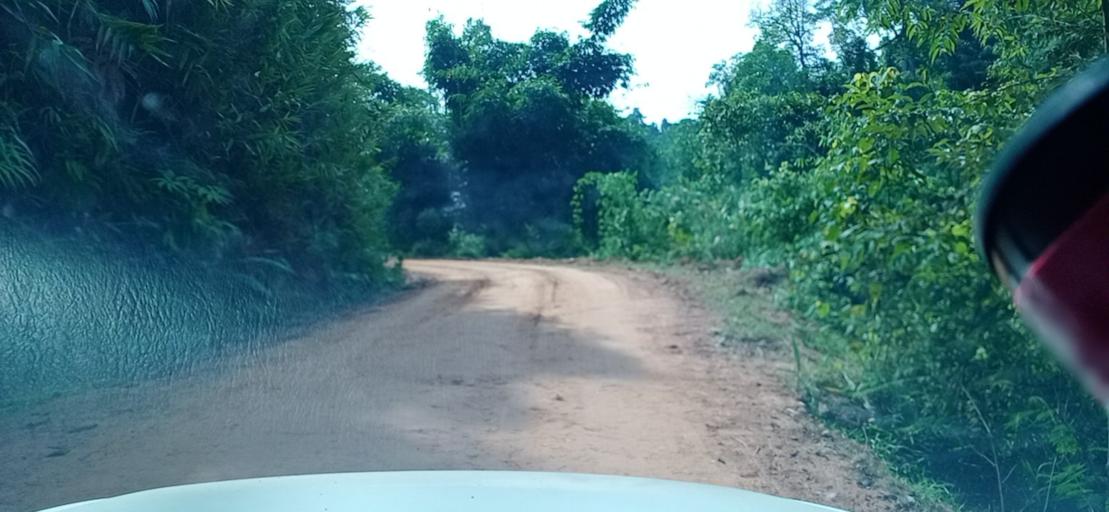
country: TH
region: Changwat Bueng Kan
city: Pak Khat
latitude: 18.6366
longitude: 103.2591
